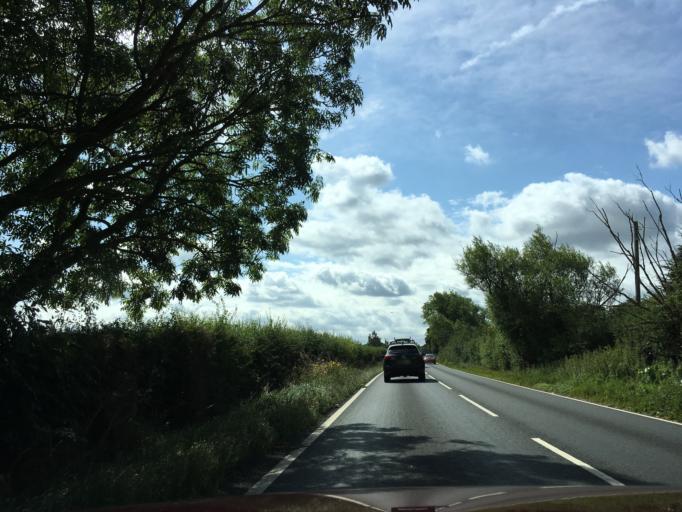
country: GB
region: England
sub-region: Kent
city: Staplehurst
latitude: 51.1434
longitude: 0.5520
